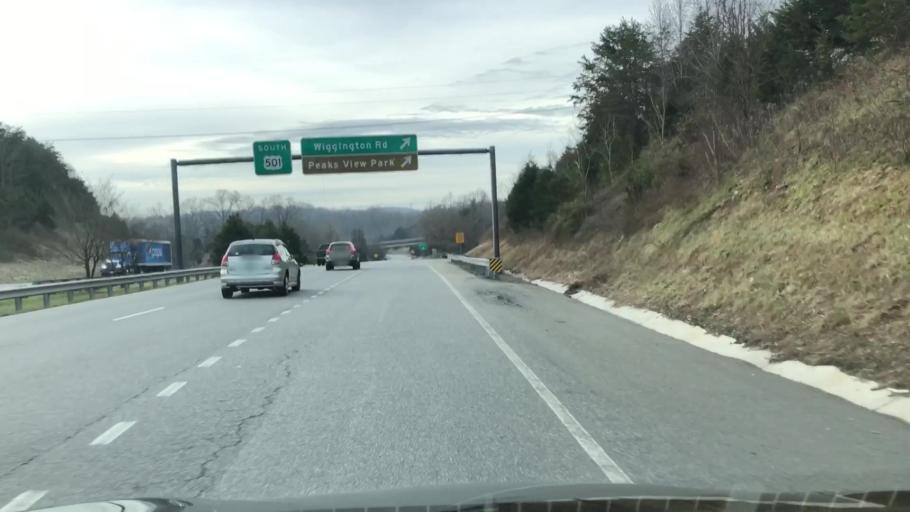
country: US
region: Virginia
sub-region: City of Lynchburg
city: West Lynchburg
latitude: 37.4193
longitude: -79.2314
